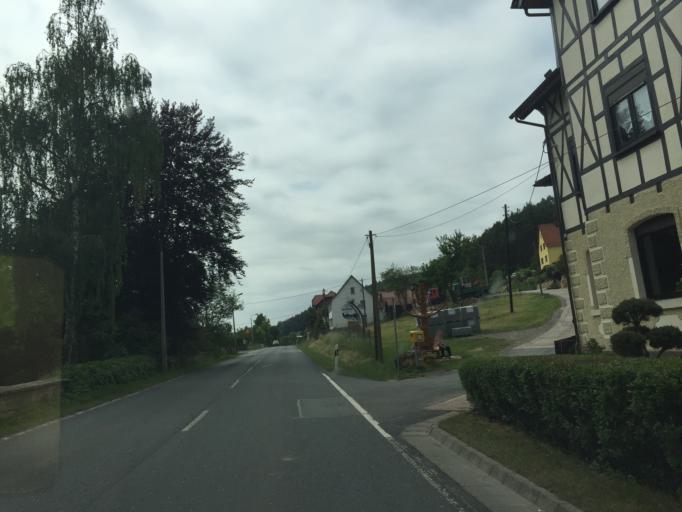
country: DE
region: Thuringia
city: Allendorf
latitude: 50.6709
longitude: 11.1442
